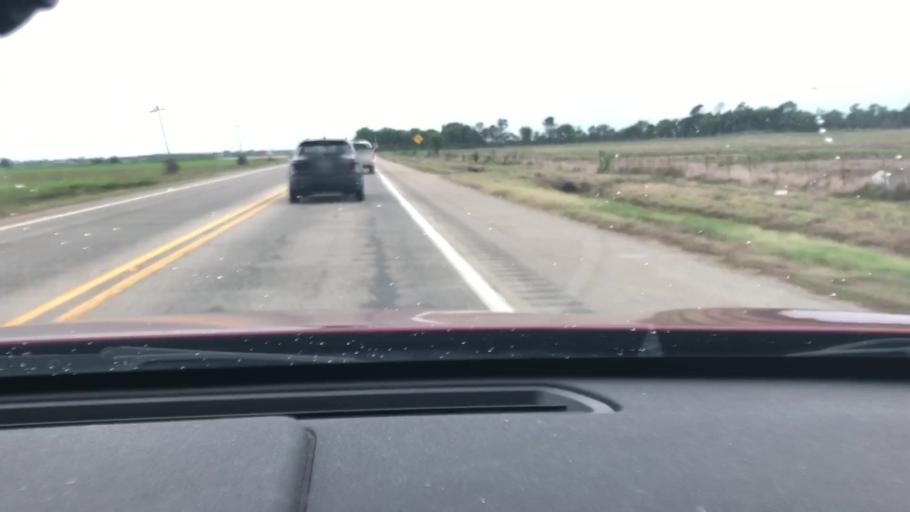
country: US
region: Arkansas
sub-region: Lafayette County
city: Lewisville
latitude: 33.4012
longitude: -93.7445
